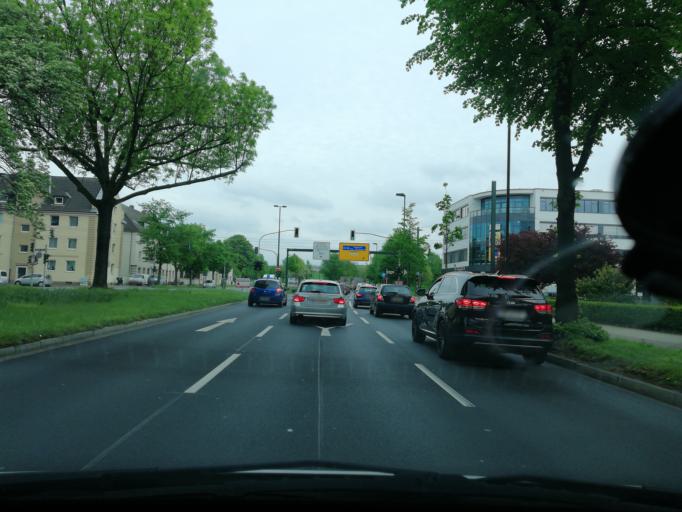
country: DE
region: North Rhine-Westphalia
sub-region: Regierungsbezirk Dusseldorf
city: Dusseldorf
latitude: 51.2001
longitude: 6.7697
